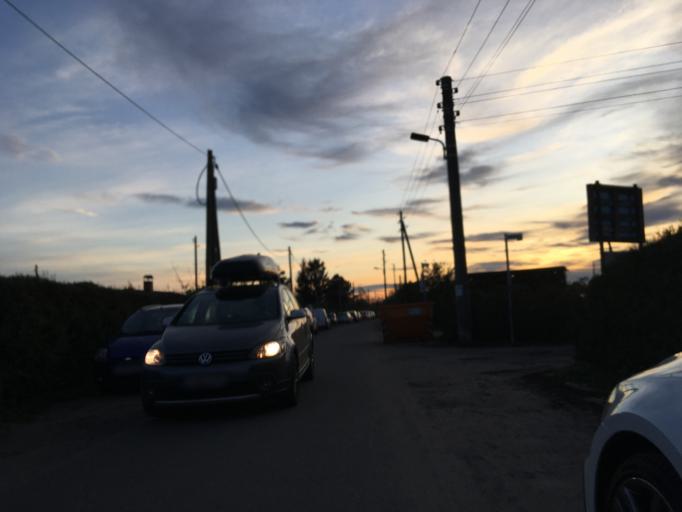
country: DE
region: Berlin
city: Buchholz
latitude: 52.6184
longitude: 13.4176
